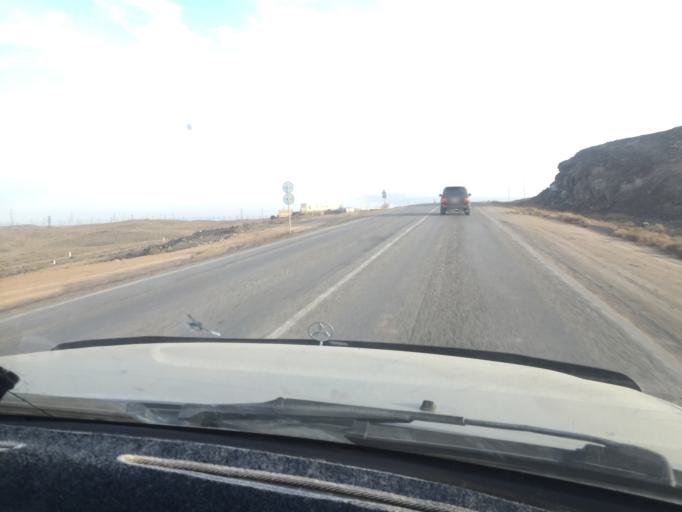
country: KZ
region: Almaty Oblysy
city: Ulken
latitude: 45.2049
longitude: 73.8862
